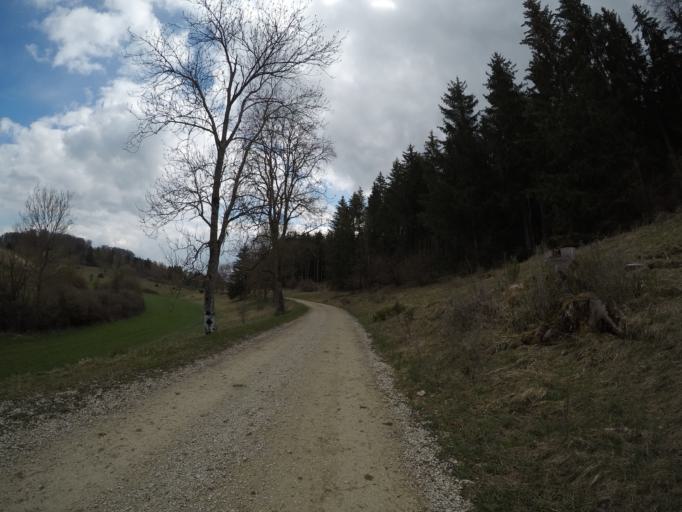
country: DE
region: Baden-Wuerttemberg
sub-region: Tuebingen Region
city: Merklingen
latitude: 48.5083
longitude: 9.7725
